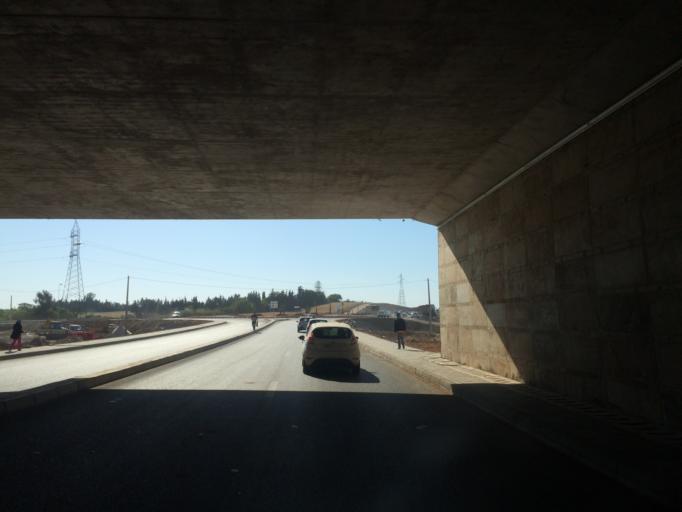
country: MA
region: Rabat-Sale-Zemmour-Zaer
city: Sale
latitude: 33.9778
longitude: -6.7368
